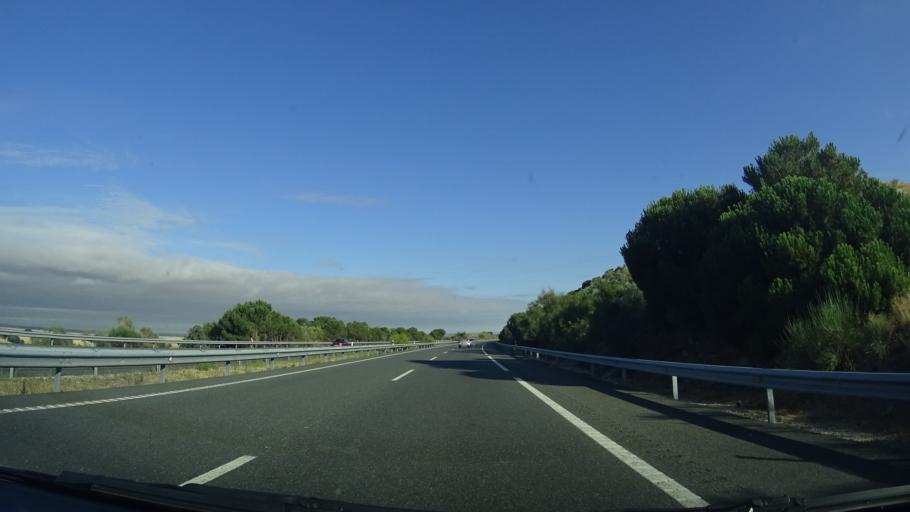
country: ES
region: Castille and Leon
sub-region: Provincia de Segovia
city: Labajos
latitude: 40.8394
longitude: -4.5347
